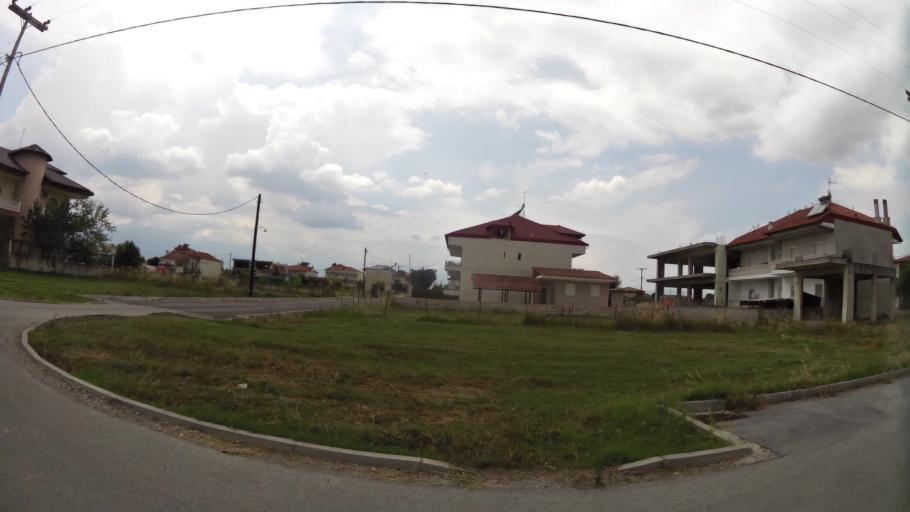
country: GR
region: Central Macedonia
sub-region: Nomos Pierias
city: Paralia
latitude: 40.2755
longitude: 22.5947
